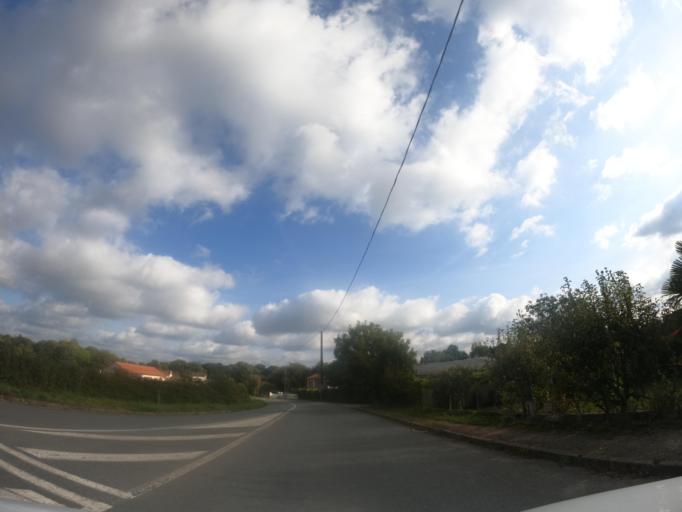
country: FR
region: Poitou-Charentes
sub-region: Departement des Deux-Sevres
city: Courlay
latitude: 46.7889
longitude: -0.6093
